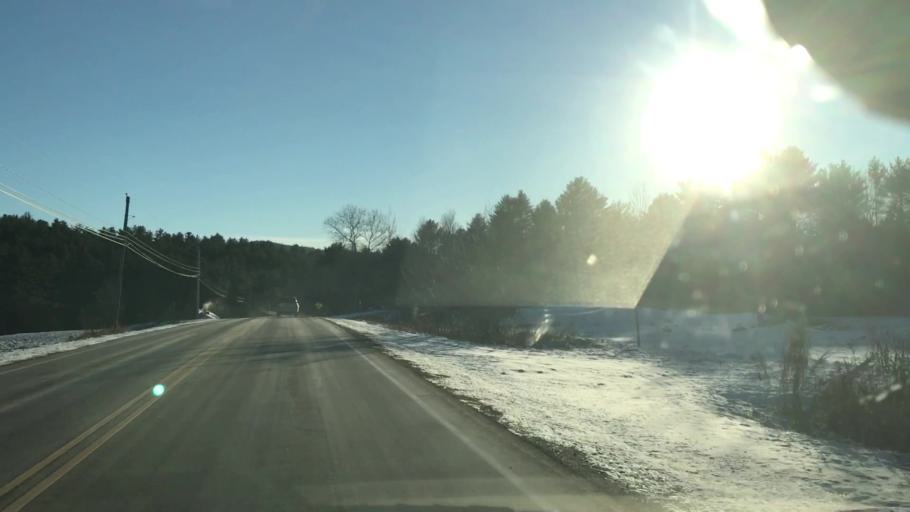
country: US
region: New Hampshire
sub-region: Grafton County
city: Haverhill
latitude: 43.9649
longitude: -72.0823
